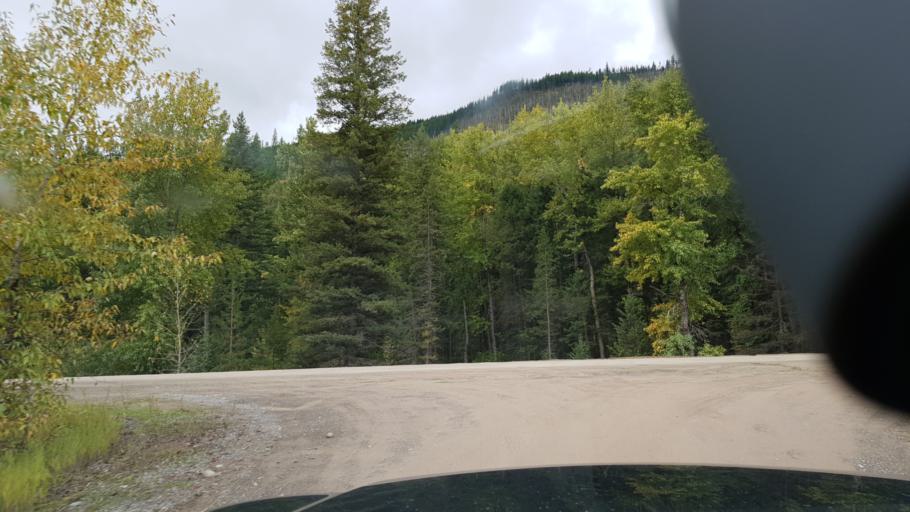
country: US
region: Montana
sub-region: Flathead County
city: Columbia Falls
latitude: 48.5676
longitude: -114.1316
